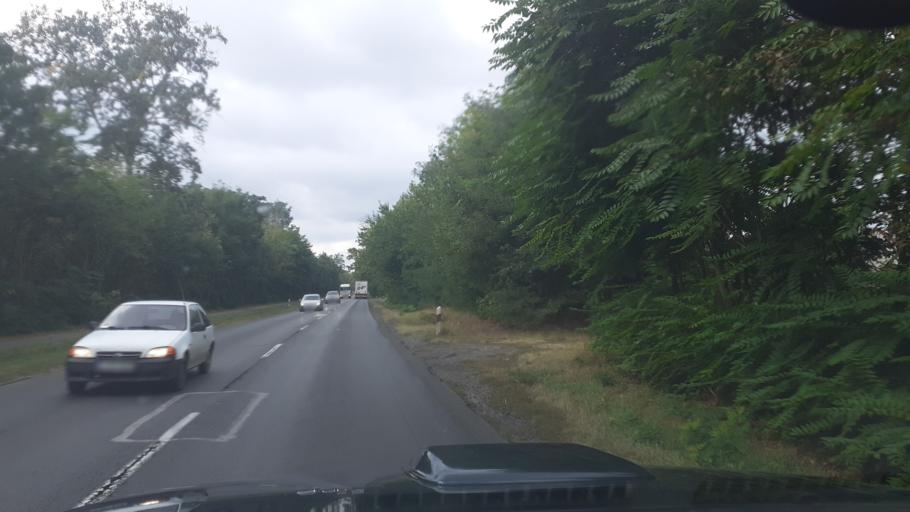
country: HU
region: Bacs-Kiskun
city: Balloszog
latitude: 46.8878
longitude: 19.6110
